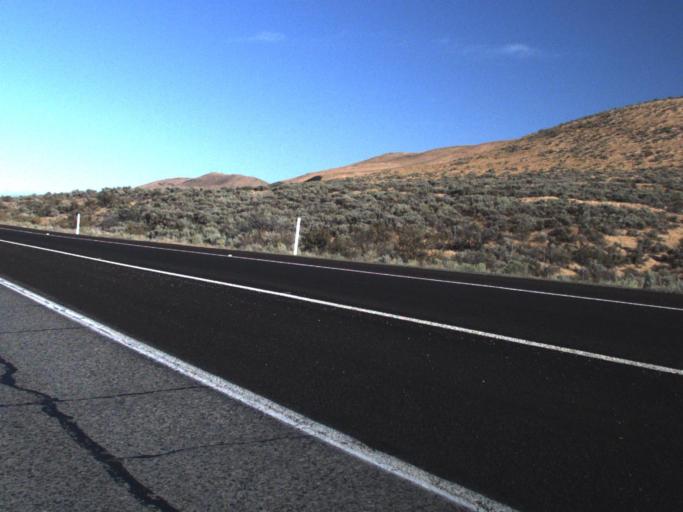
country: US
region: Washington
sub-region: Kittitas County
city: Kittitas
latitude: 46.8460
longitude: -120.3808
